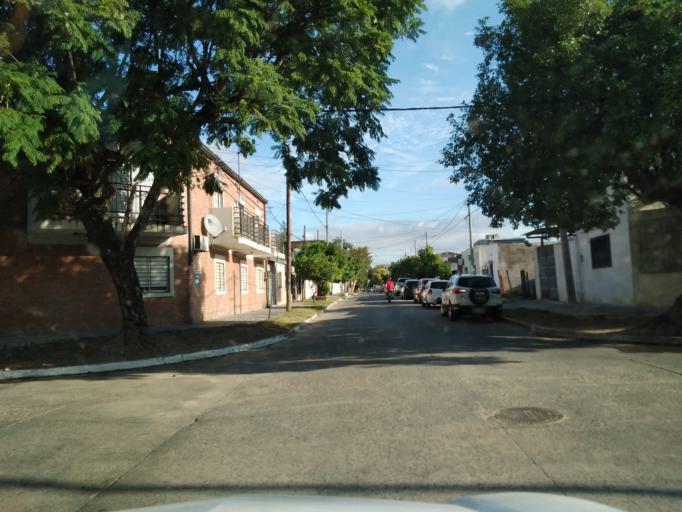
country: AR
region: Corrientes
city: Corrientes
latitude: -27.4631
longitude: -58.8206
